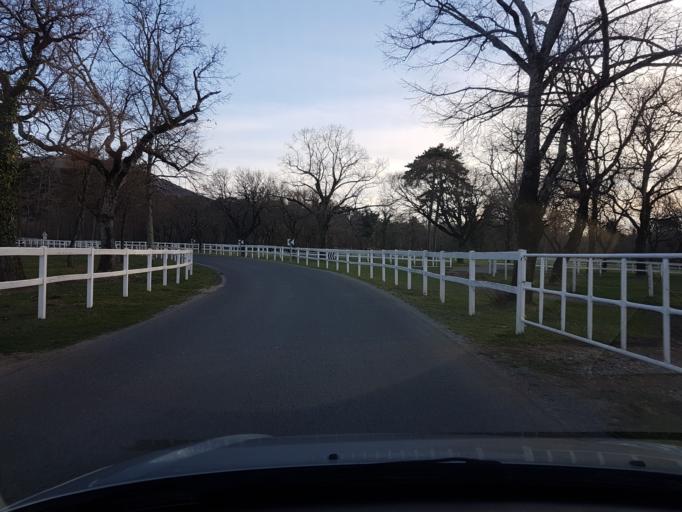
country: SI
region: Sezana
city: Sezana
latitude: 45.6609
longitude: 13.8897
